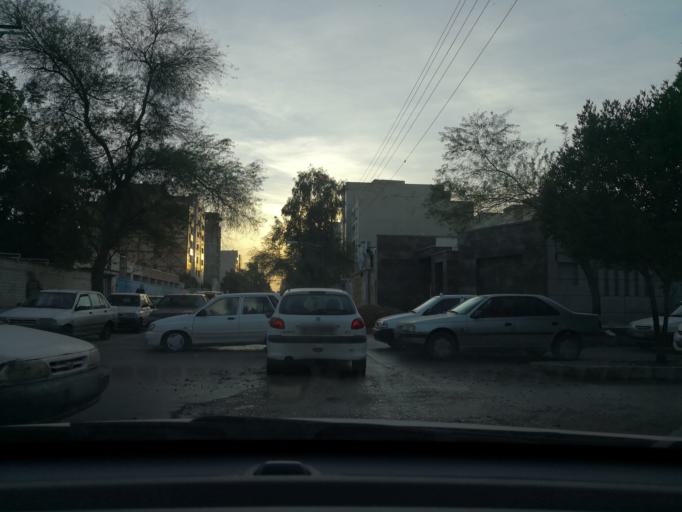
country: IR
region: Khuzestan
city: Ahvaz
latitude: 31.3514
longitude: 48.6824
